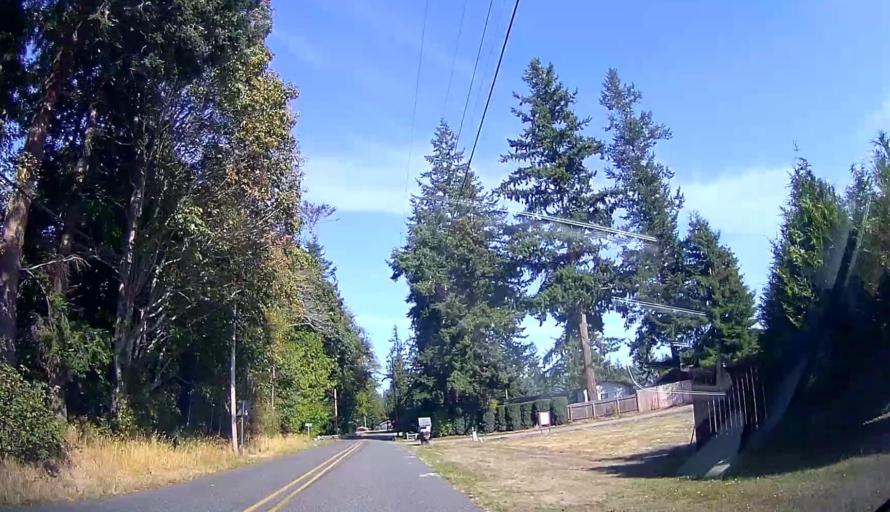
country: US
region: Washington
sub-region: Island County
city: Camano
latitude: 48.1760
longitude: -122.5228
